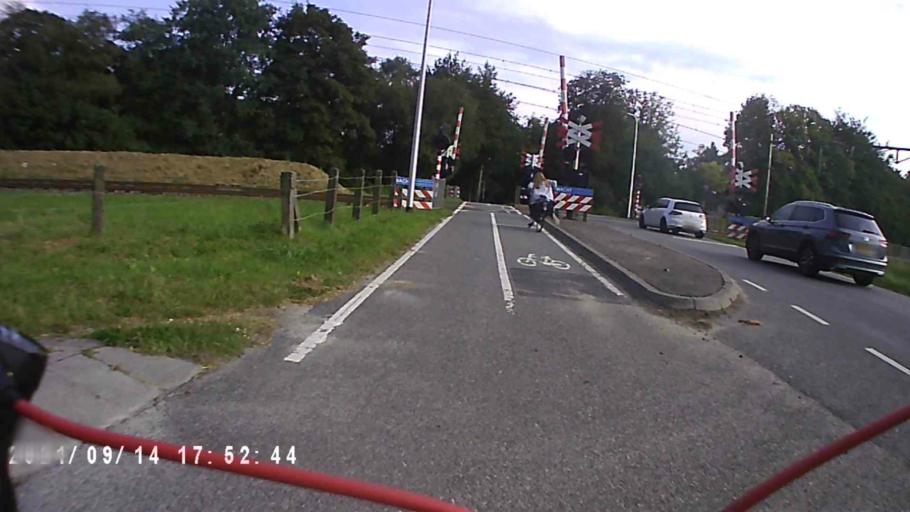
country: NL
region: Groningen
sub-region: Gemeente Haren
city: Haren
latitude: 53.1324
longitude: 6.6313
